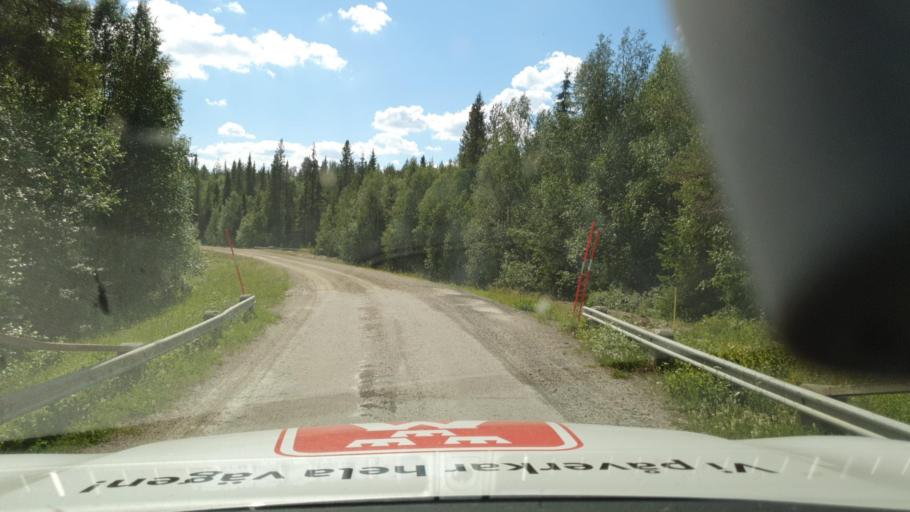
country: SE
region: Vaesterbotten
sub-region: Sorsele Kommun
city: Sorsele
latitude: 65.4493
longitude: 18.1160
